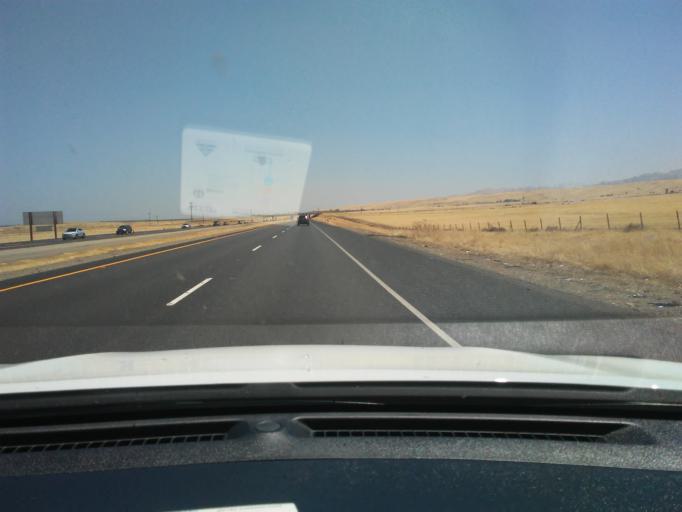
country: US
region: California
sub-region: San Joaquin County
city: Tracy
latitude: 37.6627
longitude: -121.4419
